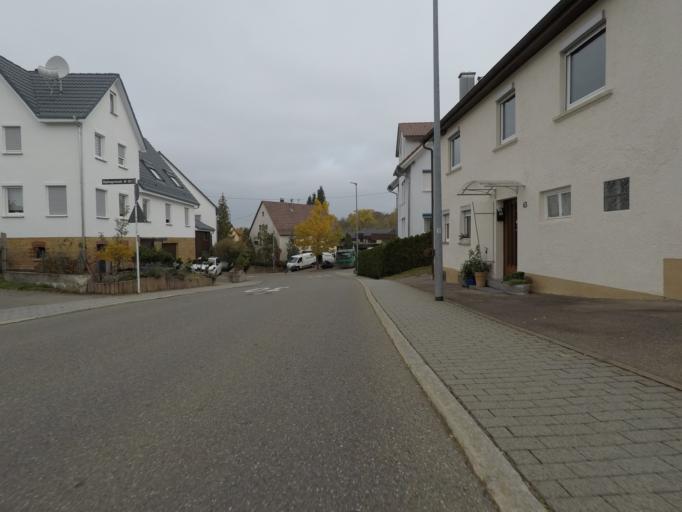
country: DE
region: Baden-Wuerttemberg
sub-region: Tuebingen Region
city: Reutlingen
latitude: 48.5176
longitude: 9.2330
